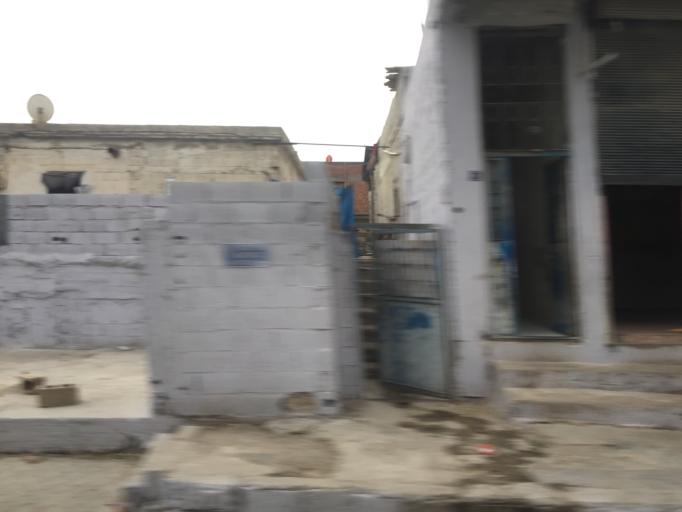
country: TR
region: Gaziantep
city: Gaziantep
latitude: 37.0715
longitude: 37.4133
